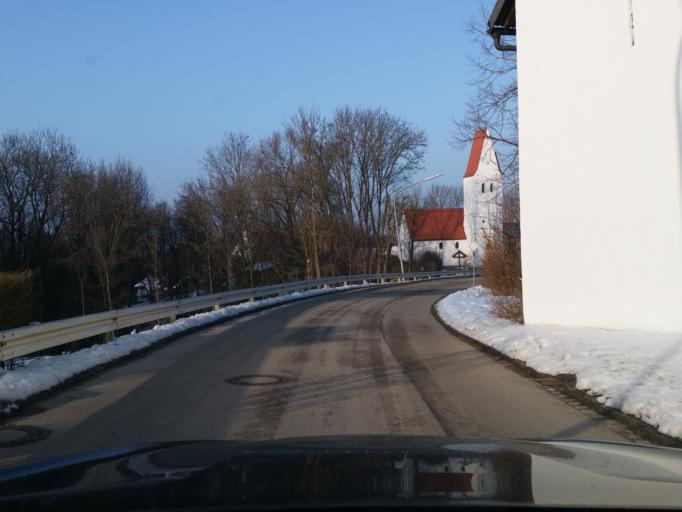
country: DE
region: Bavaria
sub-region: Lower Bavaria
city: Eching
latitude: 48.4822
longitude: 12.0302
